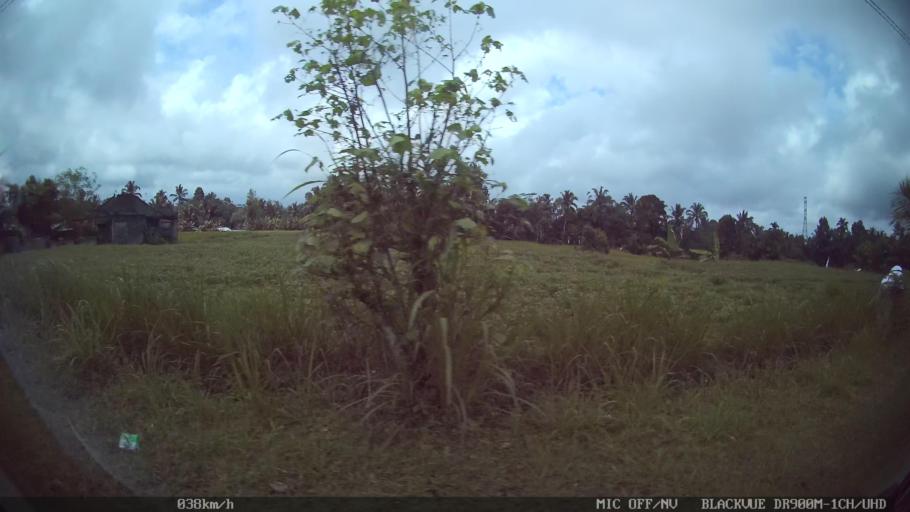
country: ID
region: Bali
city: Pemijian
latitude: -8.4382
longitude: 115.2268
